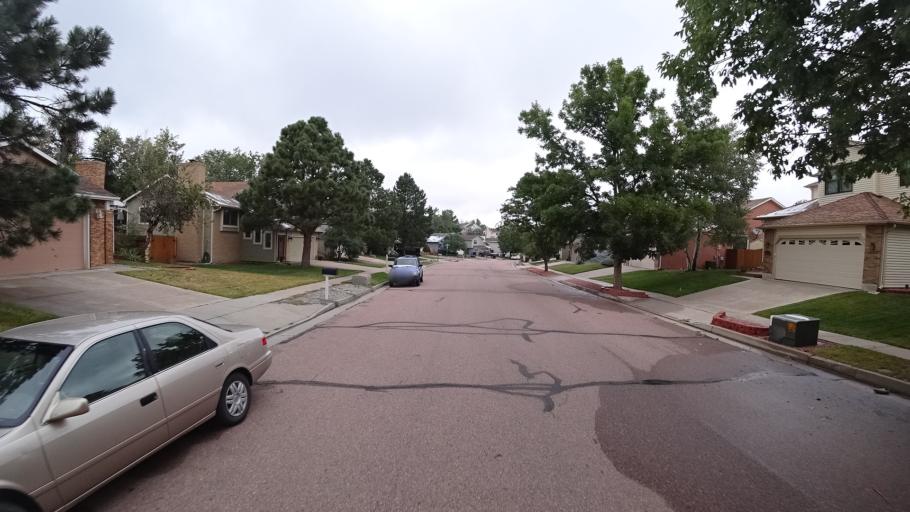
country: US
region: Colorado
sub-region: El Paso County
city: Cimarron Hills
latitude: 38.9213
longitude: -104.7614
